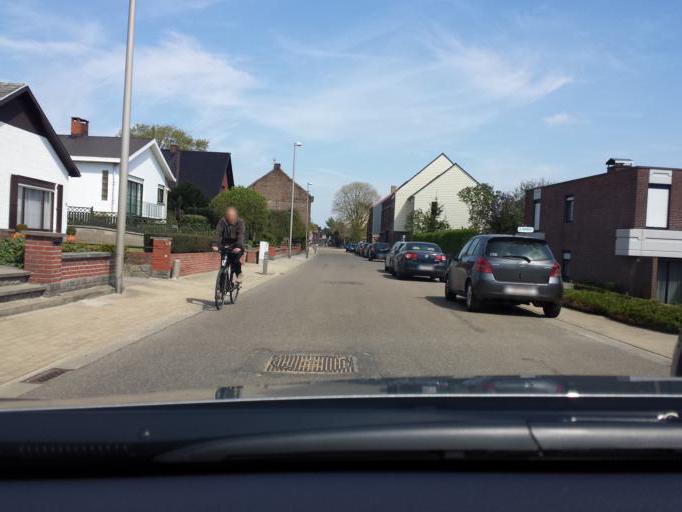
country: BE
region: Flanders
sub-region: Provincie Vlaams-Brabant
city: Kortenberg
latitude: 50.9021
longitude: 4.5515
